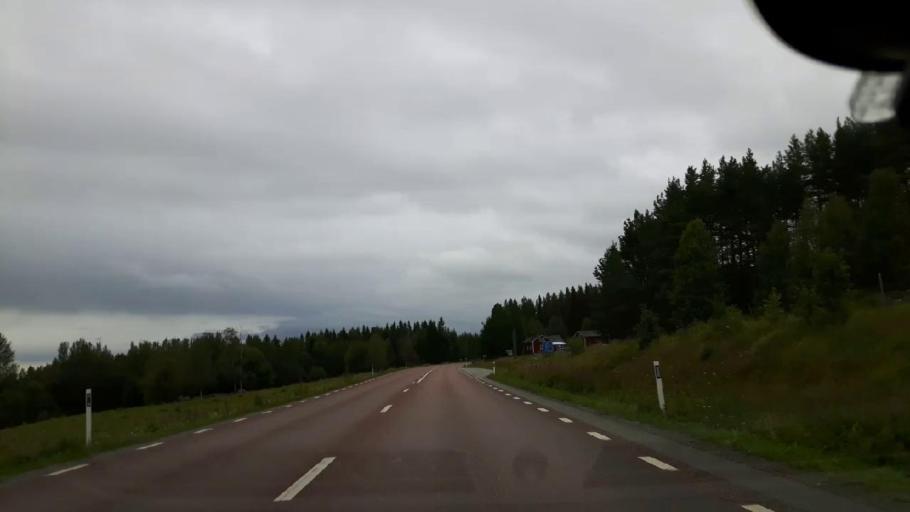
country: SE
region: Jaemtland
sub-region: Bergs Kommun
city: Hoverberg
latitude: 62.9000
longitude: 14.5226
